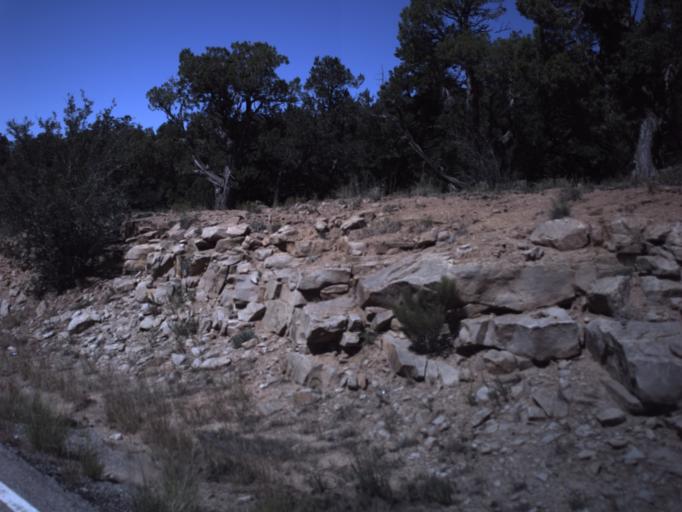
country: US
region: Utah
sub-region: Grand County
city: Moab
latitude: 38.3159
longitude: -109.2312
